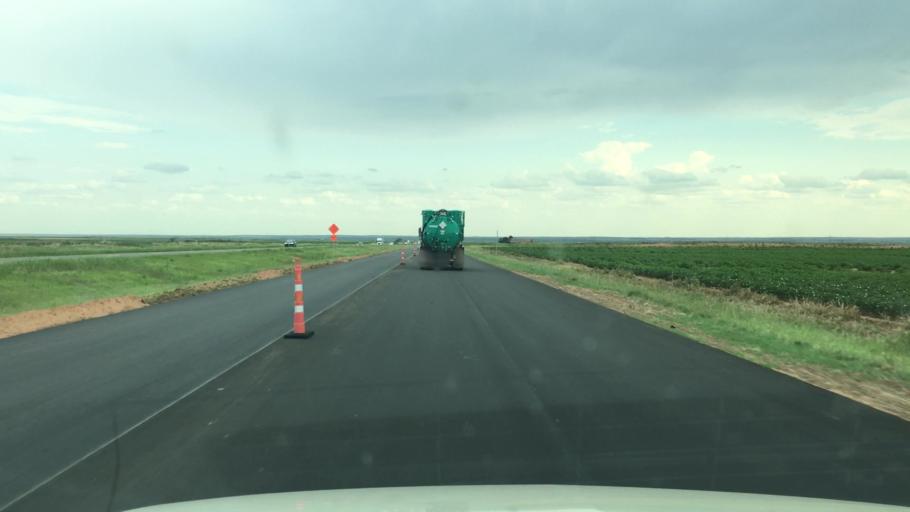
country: US
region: Texas
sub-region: Hall County
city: Memphis
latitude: 34.6257
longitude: -100.4742
